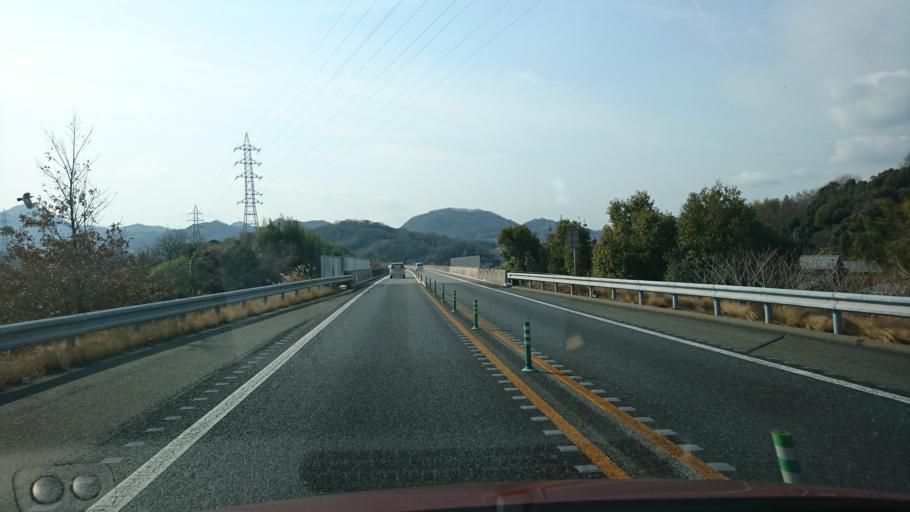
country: JP
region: Hiroshima
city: Onomichi
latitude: 34.4024
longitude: 133.2110
